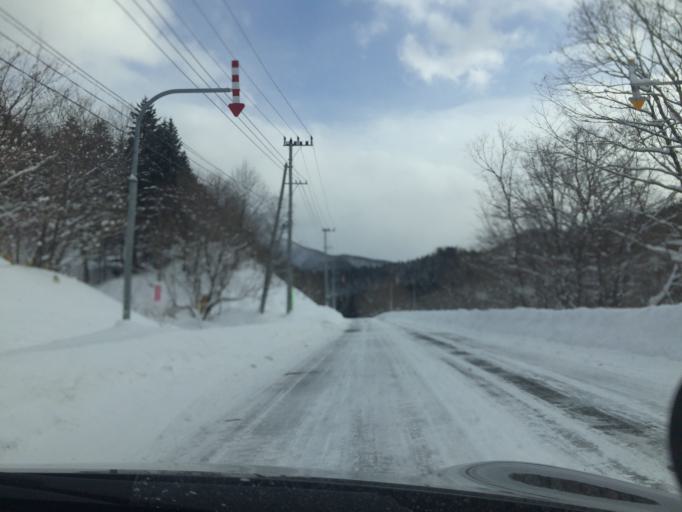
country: JP
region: Hokkaido
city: Shimo-furano
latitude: 43.0472
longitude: 142.5147
